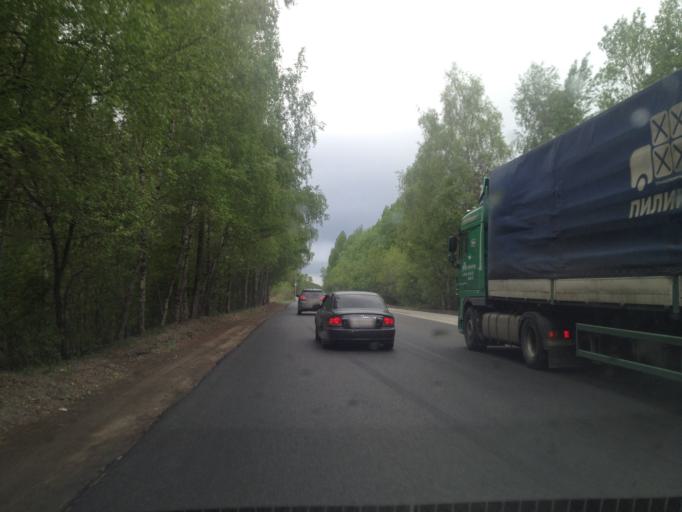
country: RU
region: Sverdlovsk
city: Sovkhoznyy
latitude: 56.8059
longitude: 60.5361
